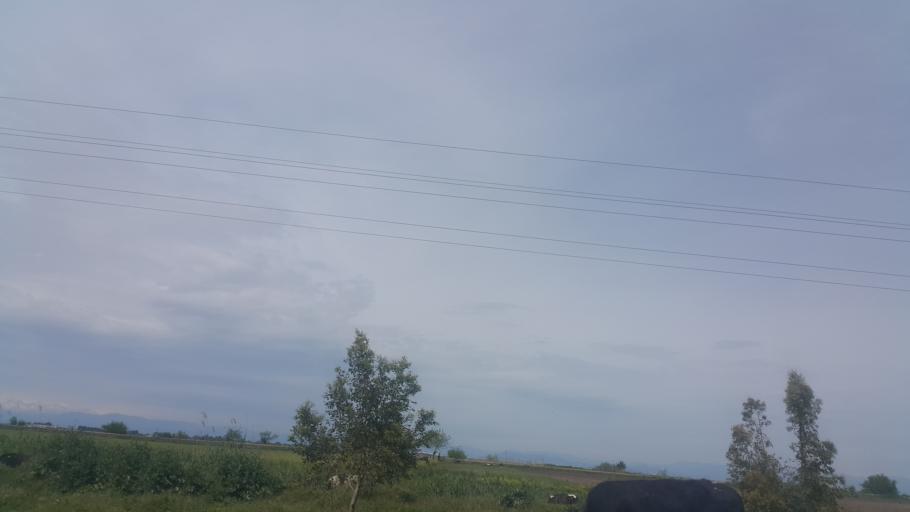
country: TR
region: Adana
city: Ceyhan
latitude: 37.0567
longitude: 35.8804
